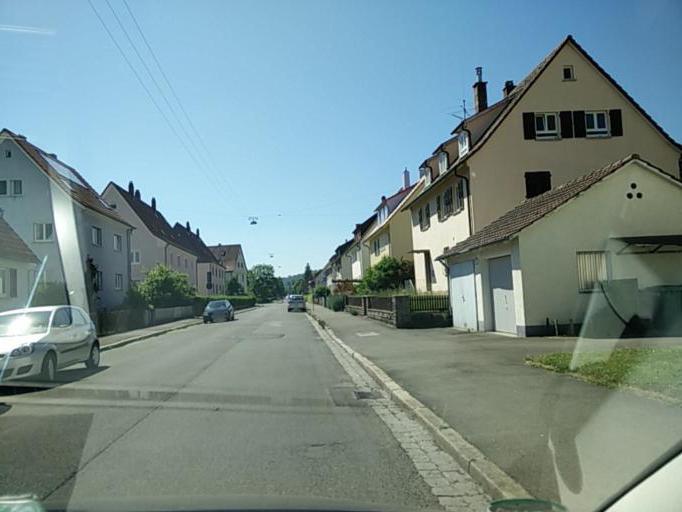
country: DE
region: Baden-Wuerttemberg
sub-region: Tuebingen Region
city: Tuebingen
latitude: 48.5084
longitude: 9.0542
